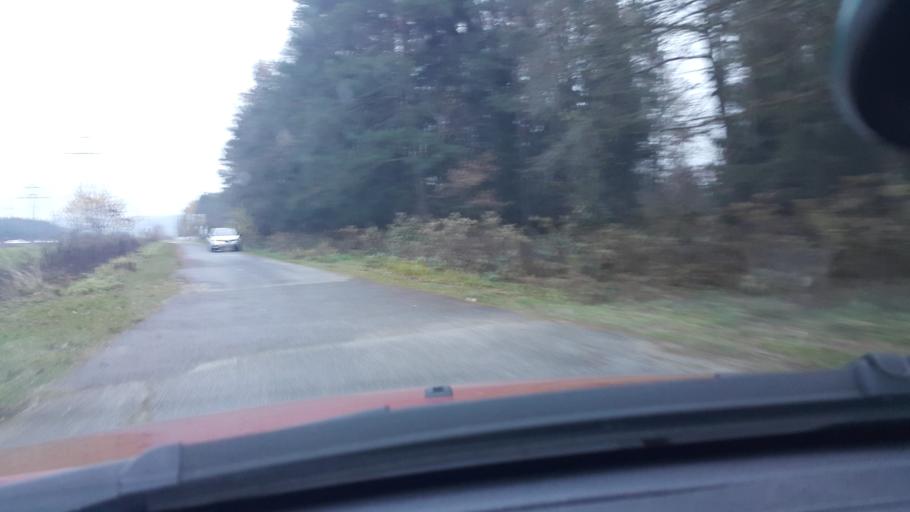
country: SI
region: Hoce-Slivnica
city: Rogoza
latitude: 46.5200
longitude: 15.6779
